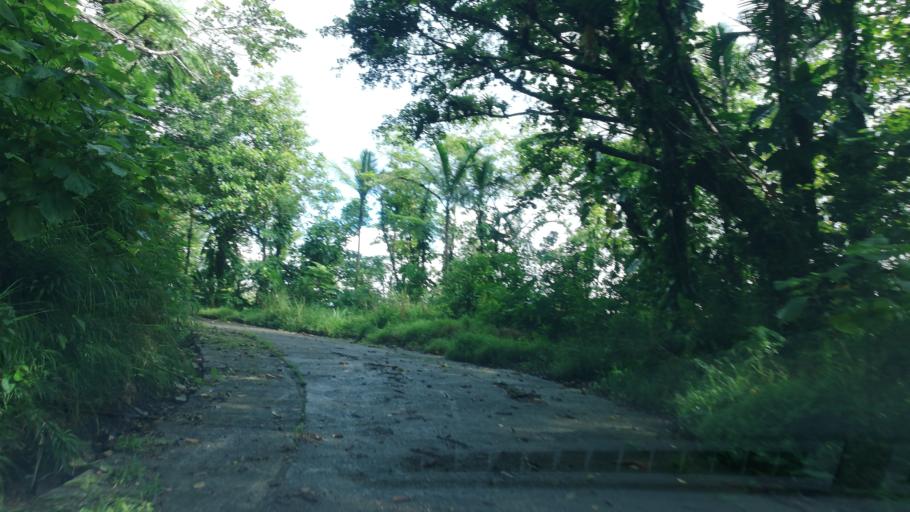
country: GP
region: Guadeloupe
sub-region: Guadeloupe
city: Bouillante
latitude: 16.1859
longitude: -61.7475
